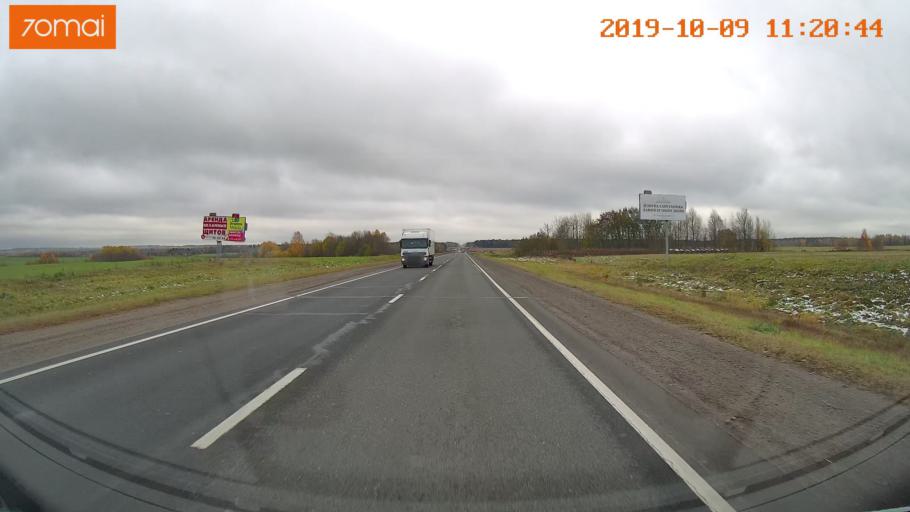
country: RU
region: Vologda
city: Vologda
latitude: 59.1462
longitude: 39.9422
